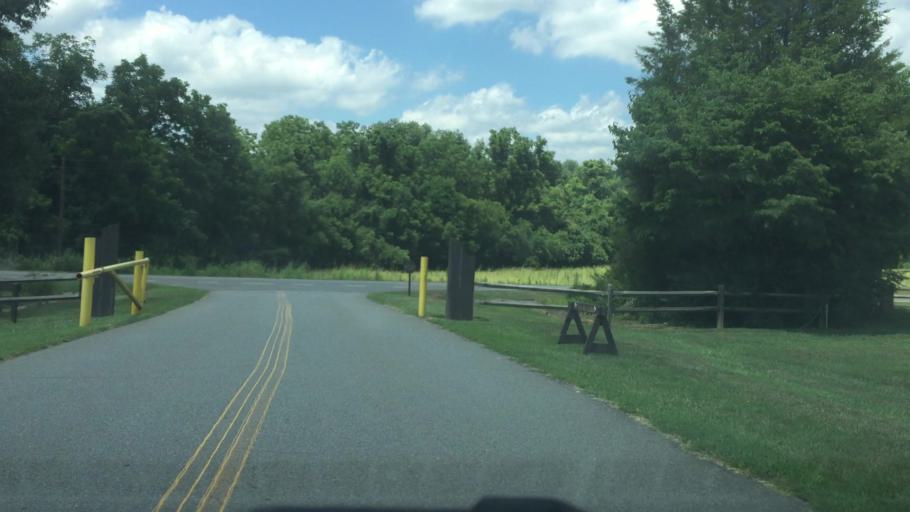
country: US
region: North Carolina
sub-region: Rowan County
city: China Grove
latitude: 35.6486
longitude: -80.6456
